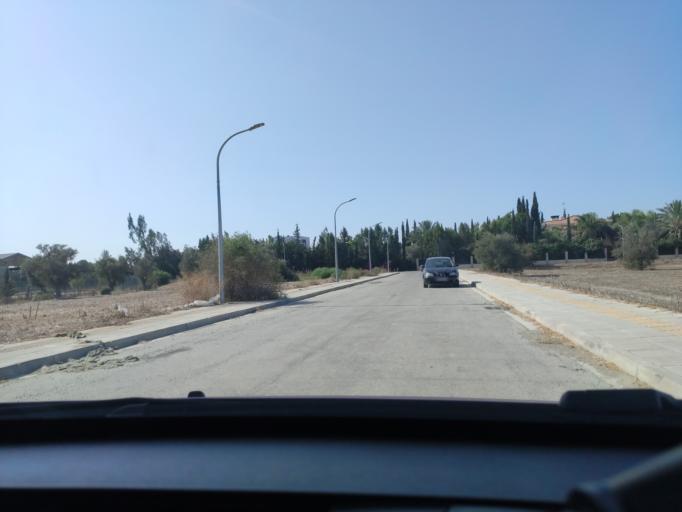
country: CY
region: Lefkosia
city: Nicosia
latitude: 35.1361
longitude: 33.3291
